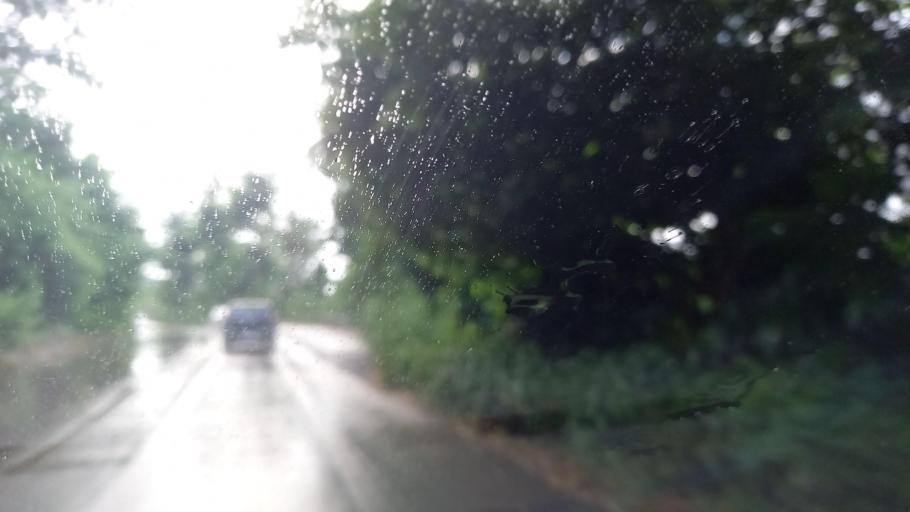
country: YT
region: Ouangani
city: Ouangani
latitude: -12.8358
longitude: 45.1481
